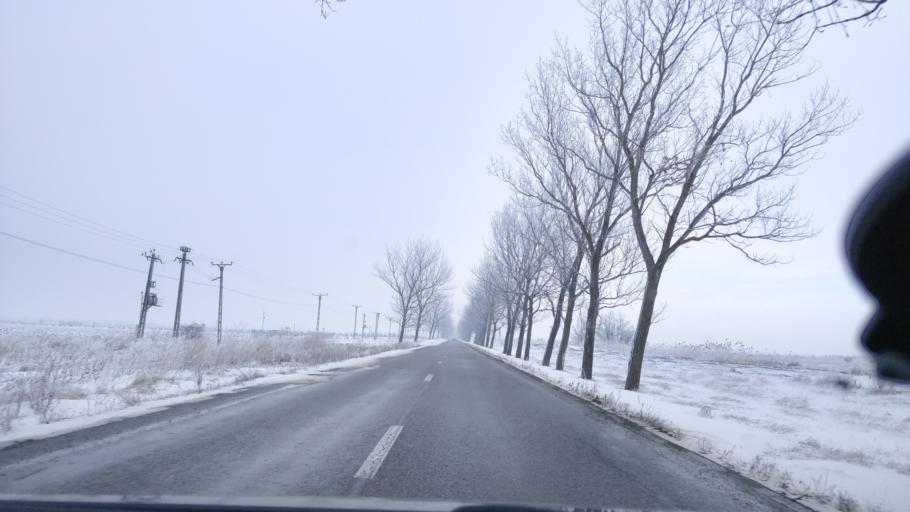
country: RO
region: Vrancea
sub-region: Comuna Vanatori
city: Jorasti
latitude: 45.6976
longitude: 27.2441
